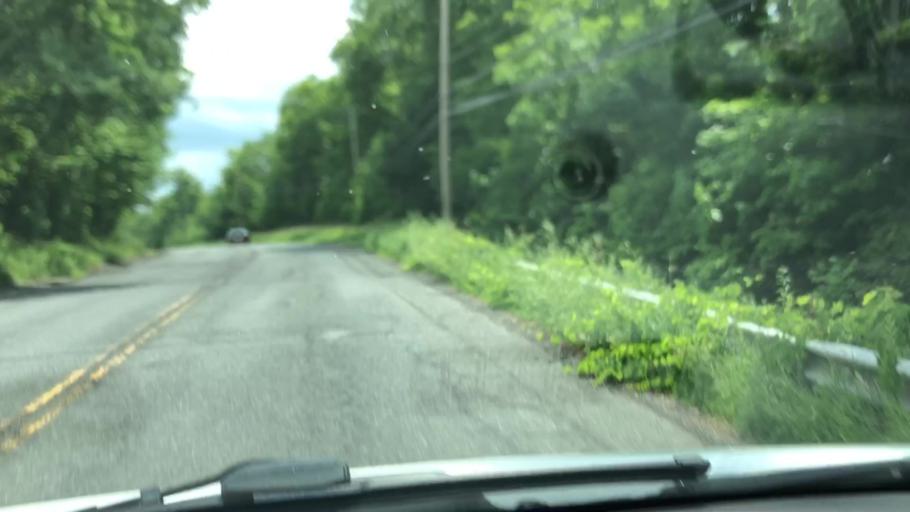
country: US
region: Massachusetts
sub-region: Berkshire County
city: Adams
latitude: 42.5942
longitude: -73.1174
